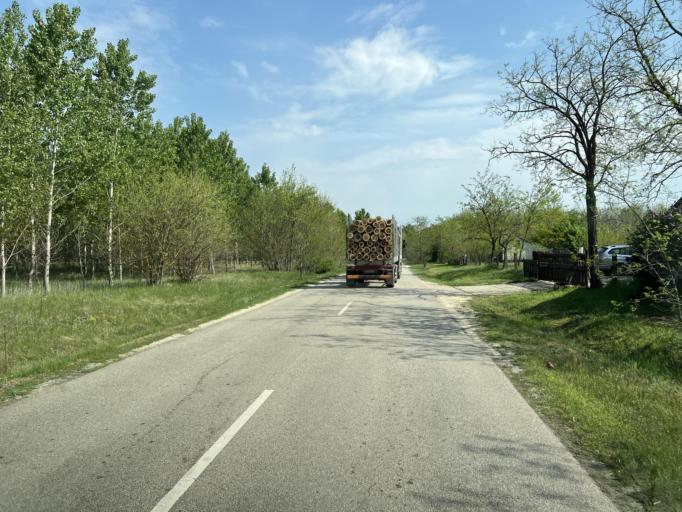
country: HU
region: Pest
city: Kocser
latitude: 47.0225
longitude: 19.9343
